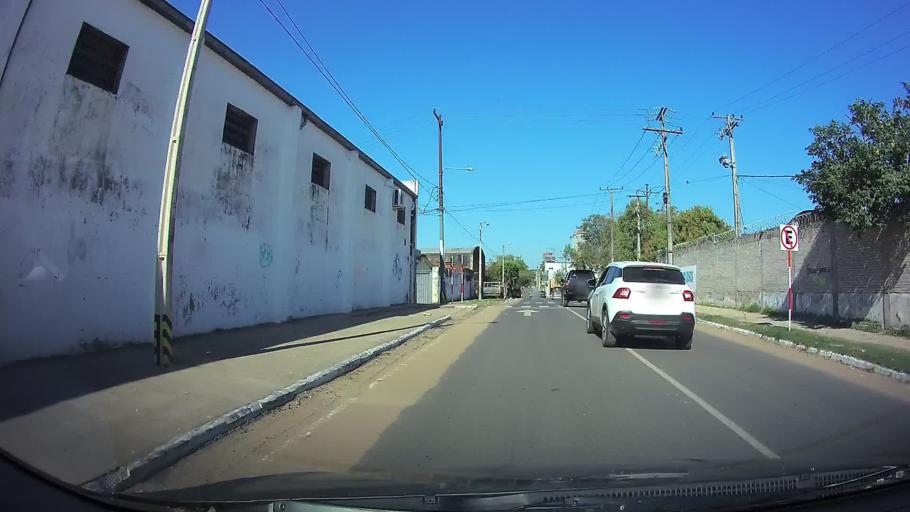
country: PY
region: Asuncion
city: Asuncion
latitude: -25.2538
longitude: -57.5833
